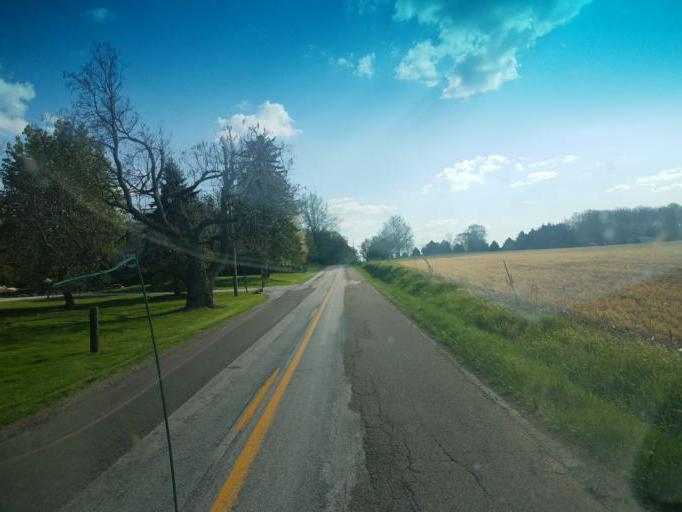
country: US
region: Ohio
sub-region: Wayne County
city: Smithville
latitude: 40.8163
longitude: -81.8667
